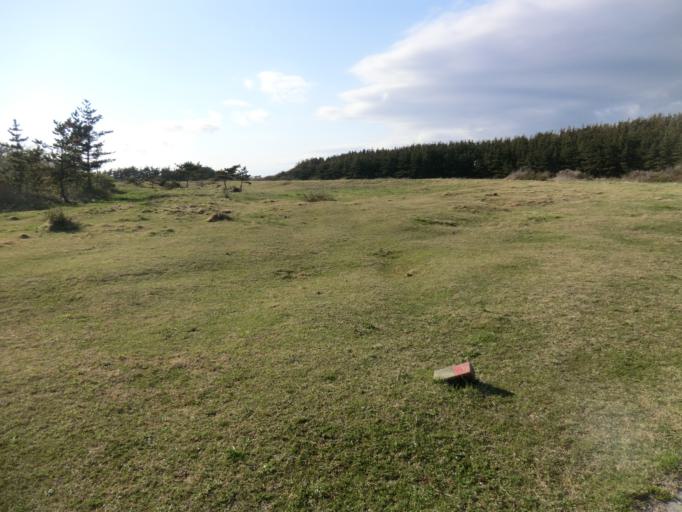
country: JP
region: Aomori
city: Mutsu
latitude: 41.4128
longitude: 141.4479
